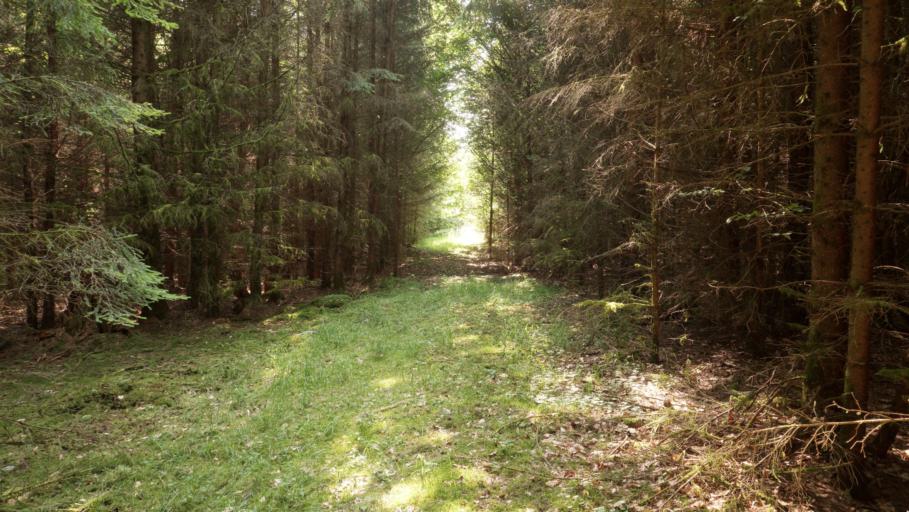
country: DE
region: Baden-Wuerttemberg
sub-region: Karlsruhe Region
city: Hassmersheim
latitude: 49.3249
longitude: 9.1782
